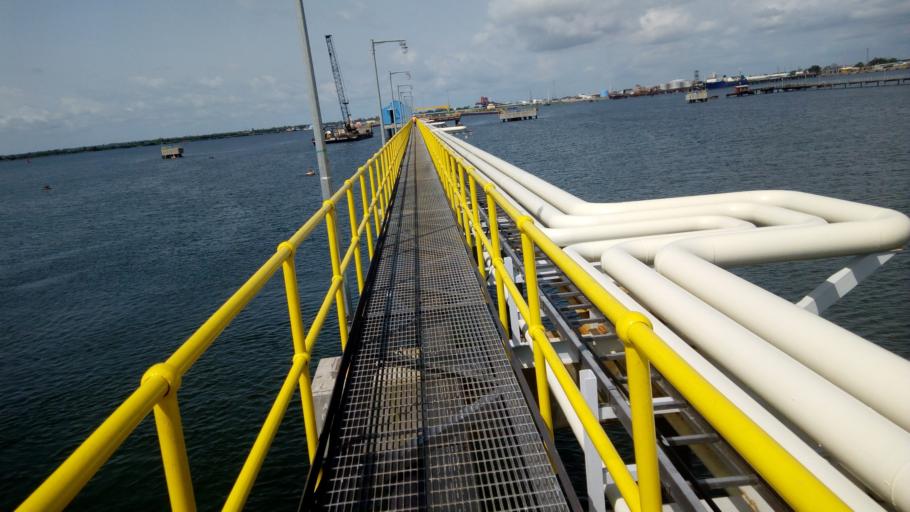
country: LR
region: Montserrado
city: Monrovia
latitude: 6.3404
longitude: -10.8035
